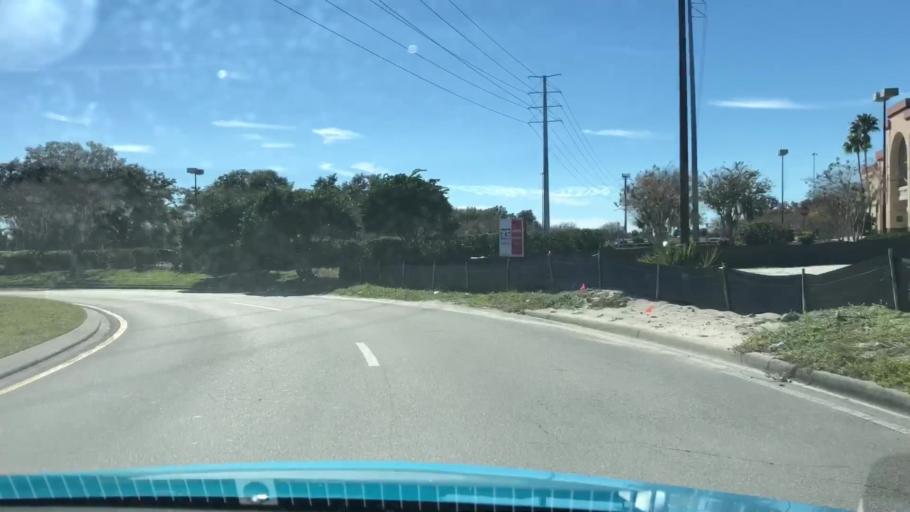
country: US
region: Florida
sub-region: Seminole County
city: Lake Mary
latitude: 28.7998
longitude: -81.3413
